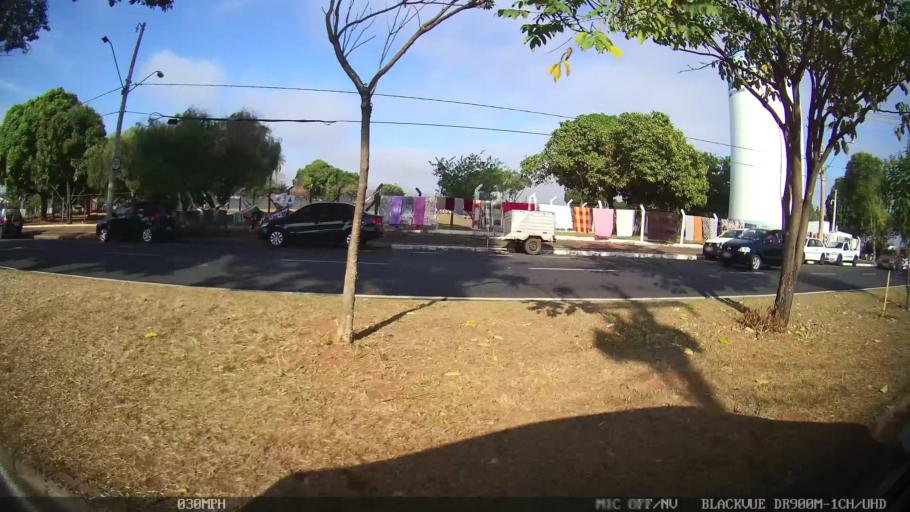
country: BR
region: Sao Paulo
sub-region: Sao Jose Do Rio Preto
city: Sao Jose do Rio Preto
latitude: -20.7925
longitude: -49.4186
